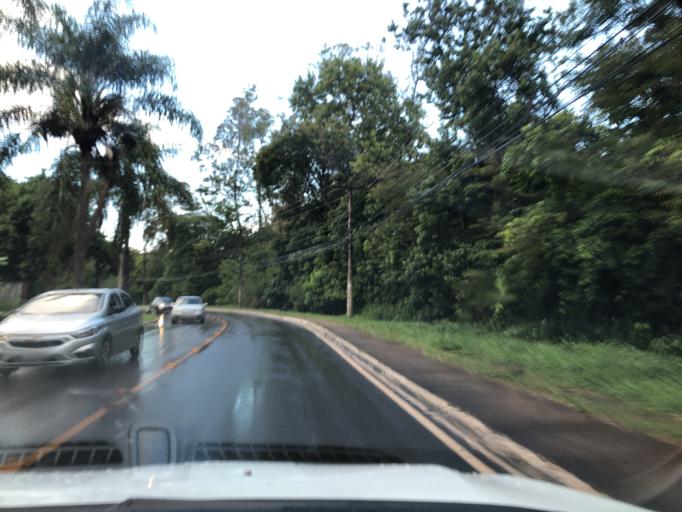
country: BR
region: Federal District
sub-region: Brasilia
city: Brasilia
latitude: -15.8753
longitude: -47.9658
